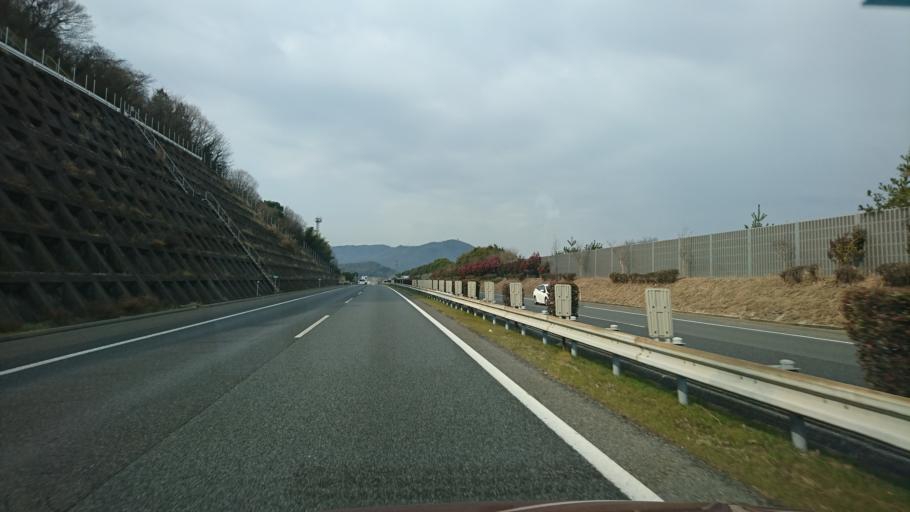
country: JP
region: Hiroshima
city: Fukuyama
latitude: 34.5169
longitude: 133.3824
